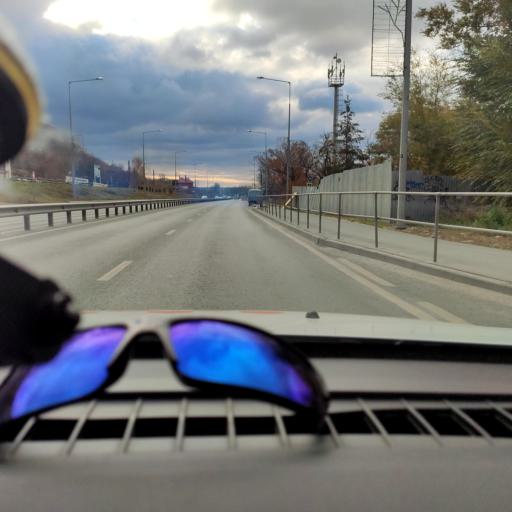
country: RU
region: Samara
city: Volzhskiy
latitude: 53.4025
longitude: 50.1475
